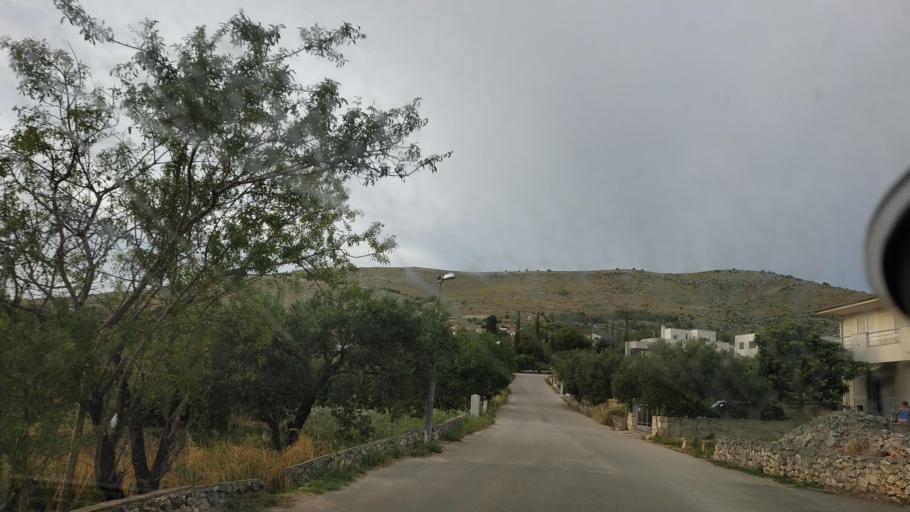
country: HR
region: Sibensko-Kniniska
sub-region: Grad Sibenik
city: Brodarica
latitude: 43.6353
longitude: 15.9642
